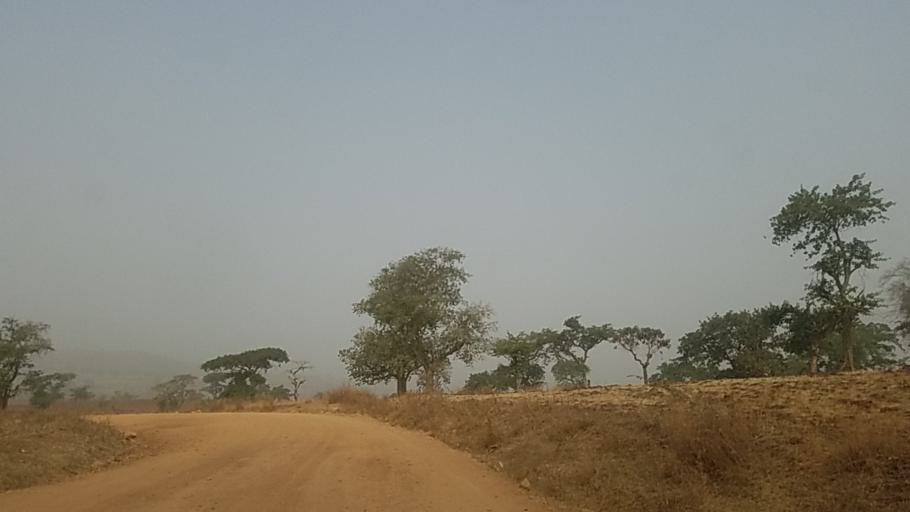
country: ET
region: Amhara
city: Bure
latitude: 10.7820
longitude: 36.2913
